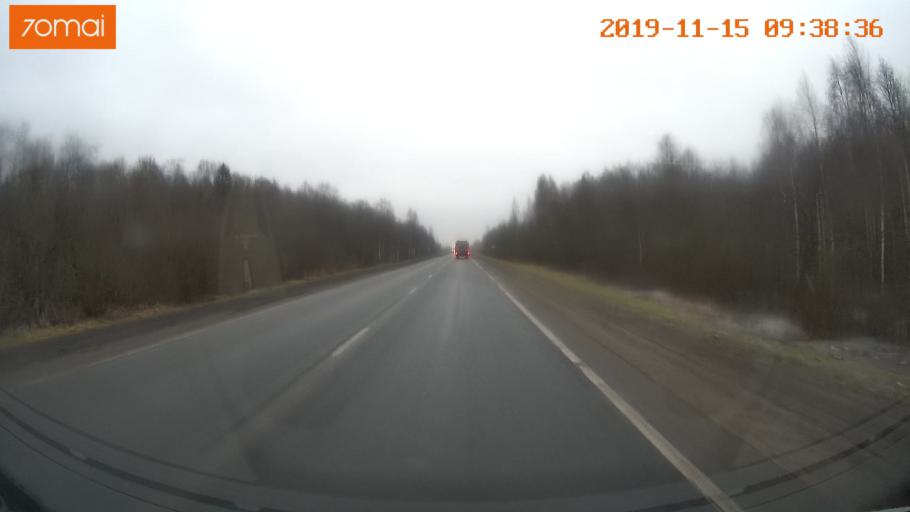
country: RU
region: Vologda
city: Sheksna
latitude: 59.2305
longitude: 38.4587
